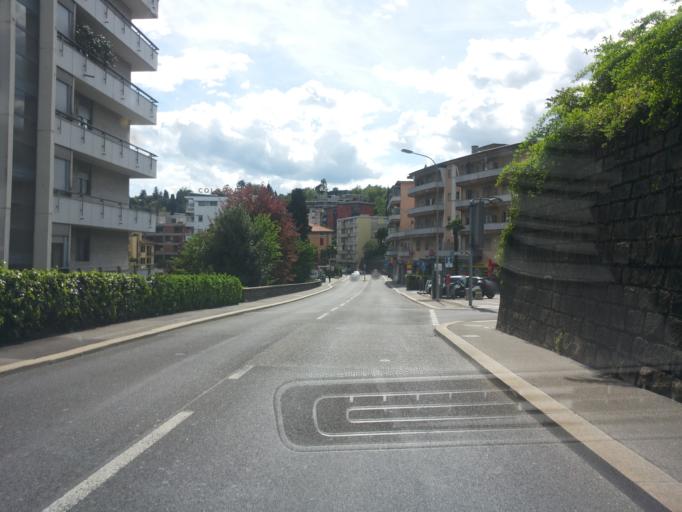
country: CH
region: Ticino
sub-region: Lugano District
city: Sorengo
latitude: 45.9991
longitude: 8.9454
